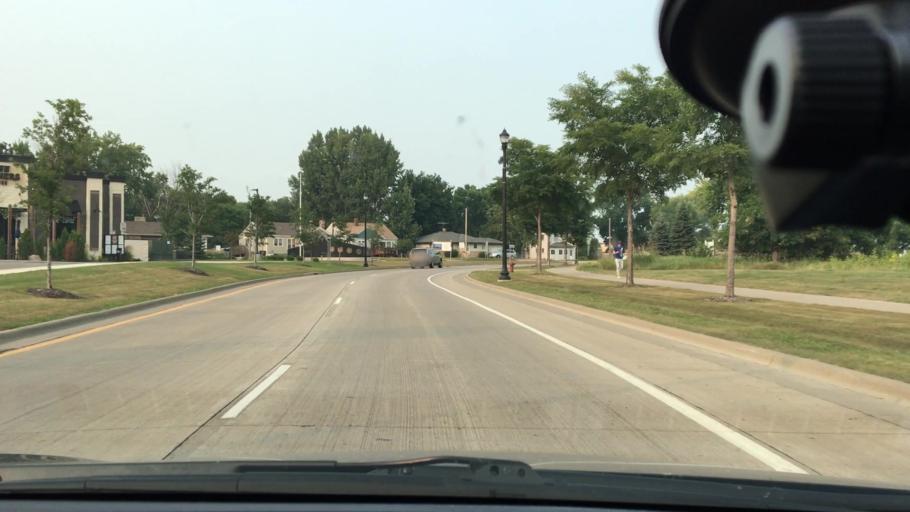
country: US
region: Minnesota
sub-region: Wright County
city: Saint Michael
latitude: 45.2092
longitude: -93.6614
